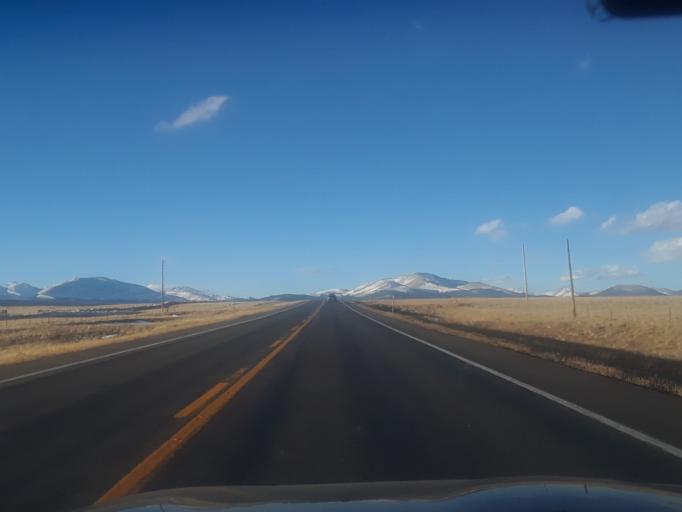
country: US
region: Colorado
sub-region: Park County
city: Fairplay
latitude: 39.1397
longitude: -105.9966
